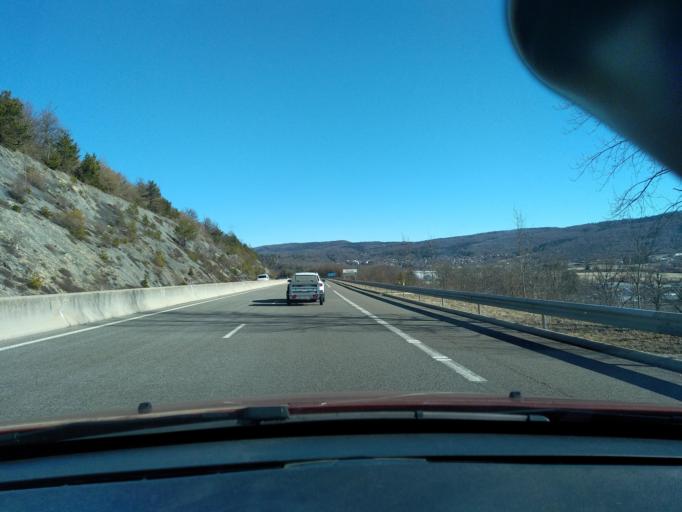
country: FR
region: Rhone-Alpes
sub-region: Departement de l'Ain
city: Oyonnax
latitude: 46.2744
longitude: 5.6537
